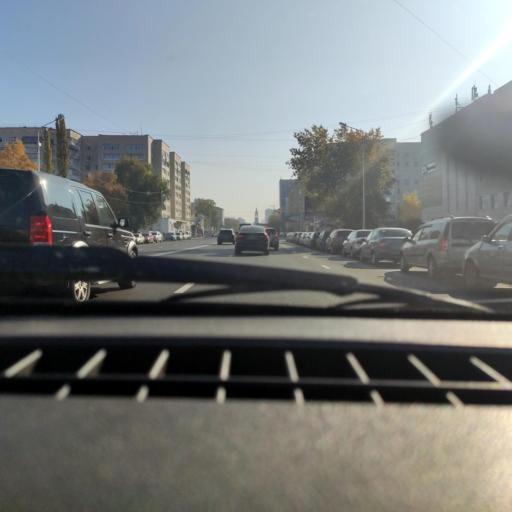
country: RU
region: Bashkortostan
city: Ufa
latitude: 54.7292
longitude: 55.9610
